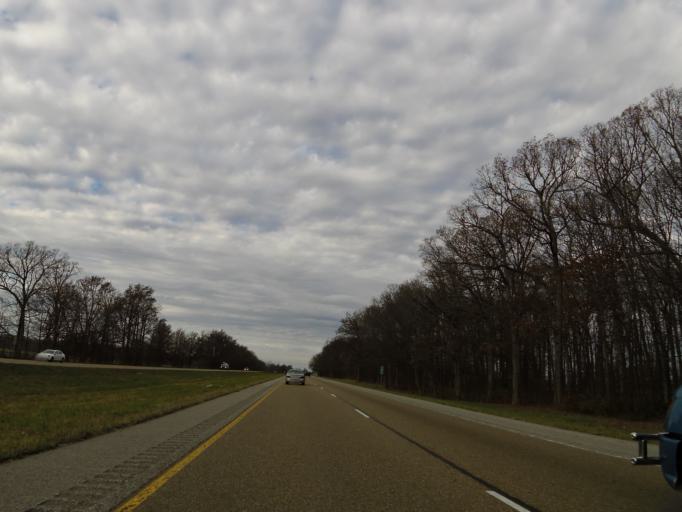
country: US
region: Illinois
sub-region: Clinton County
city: Wamac
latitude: 38.3877
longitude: -89.1502
